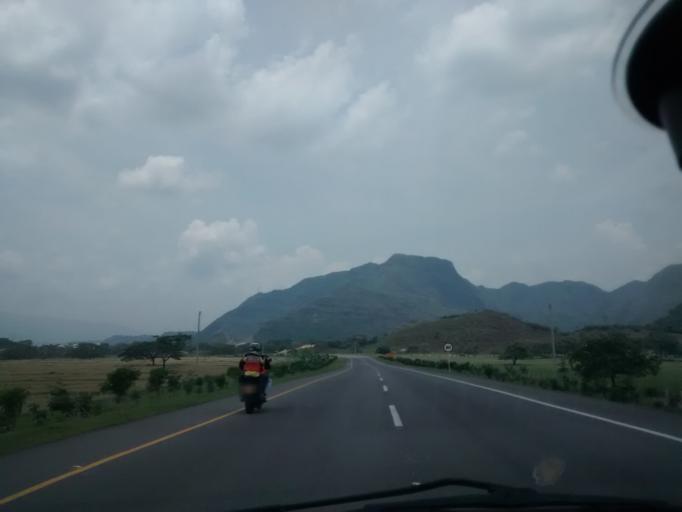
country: CO
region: Tolima
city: Valle de San Juan
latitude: 4.2758
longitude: -75.0046
